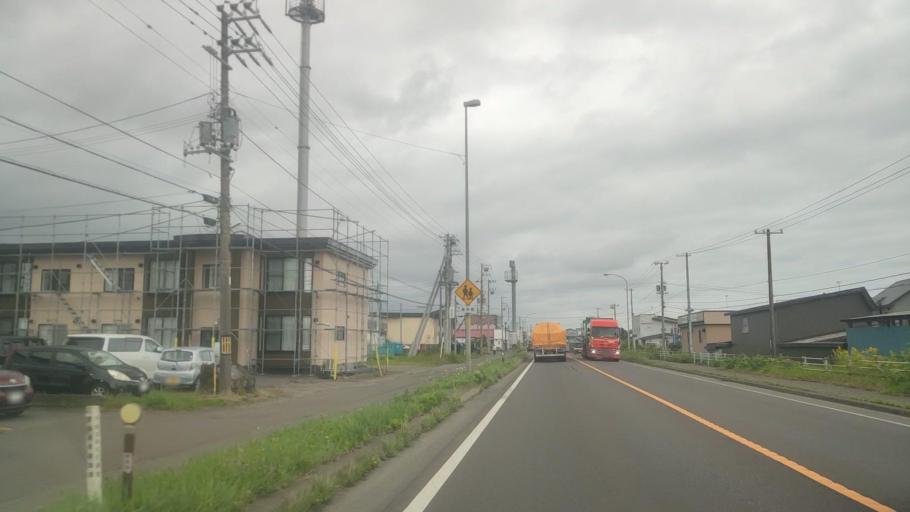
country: JP
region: Hokkaido
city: Shiraoi
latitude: 42.5174
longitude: 141.3023
